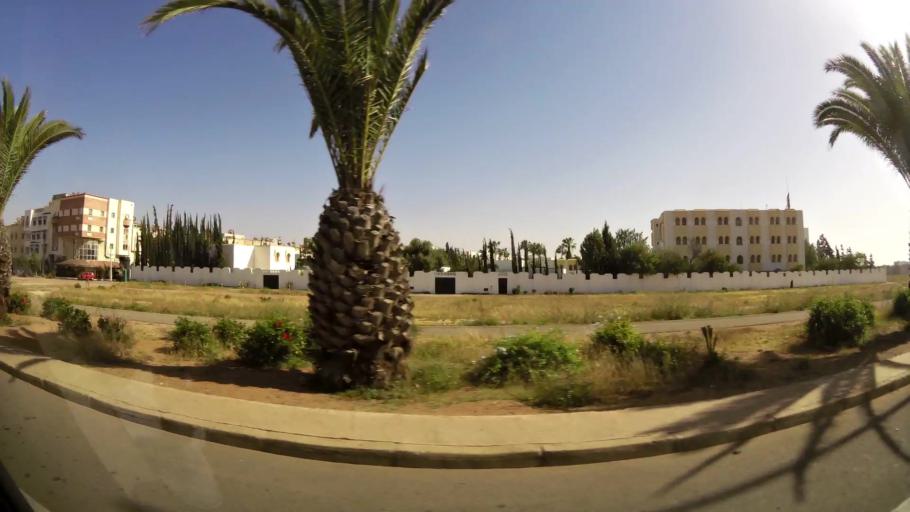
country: MA
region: Oued ed Dahab-Lagouira
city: Dakhla
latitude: 30.4039
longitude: -9.5548
